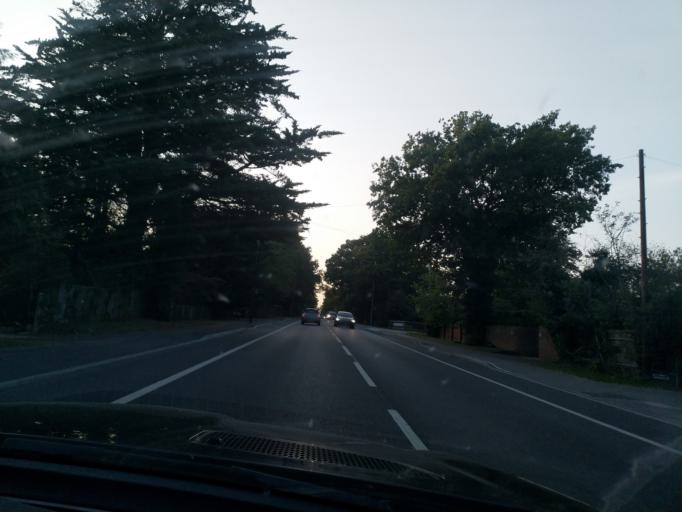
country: GB
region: England
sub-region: Kent
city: Leysdown-on-Sea
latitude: 51.4203
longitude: 0.8576
